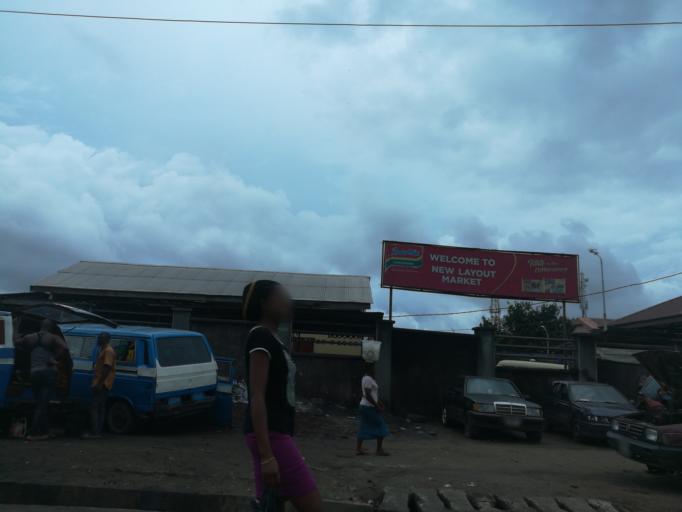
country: NG
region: Rivers
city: Port Harcourt
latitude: 4.7591
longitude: 7.0323
